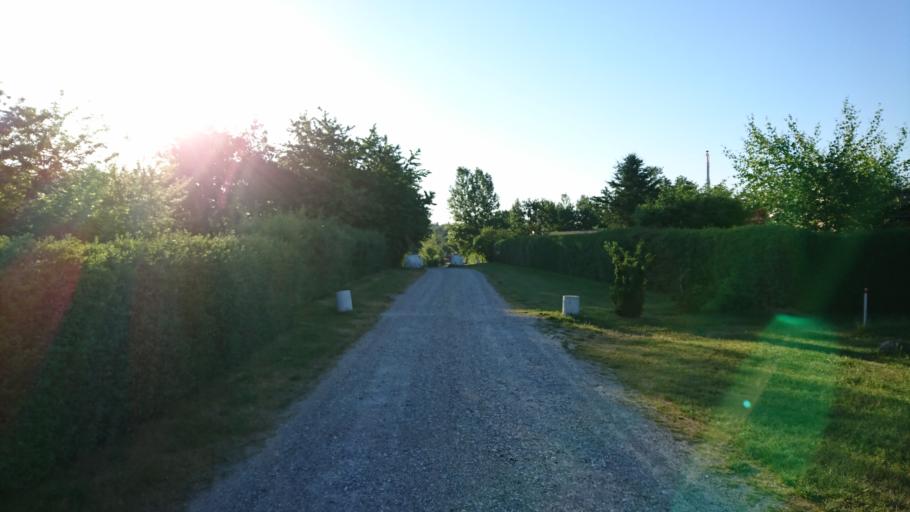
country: DK
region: Capital Region
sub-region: Egedal Kommune
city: Smorumnedre
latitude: 55.7234
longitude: 12.3266
